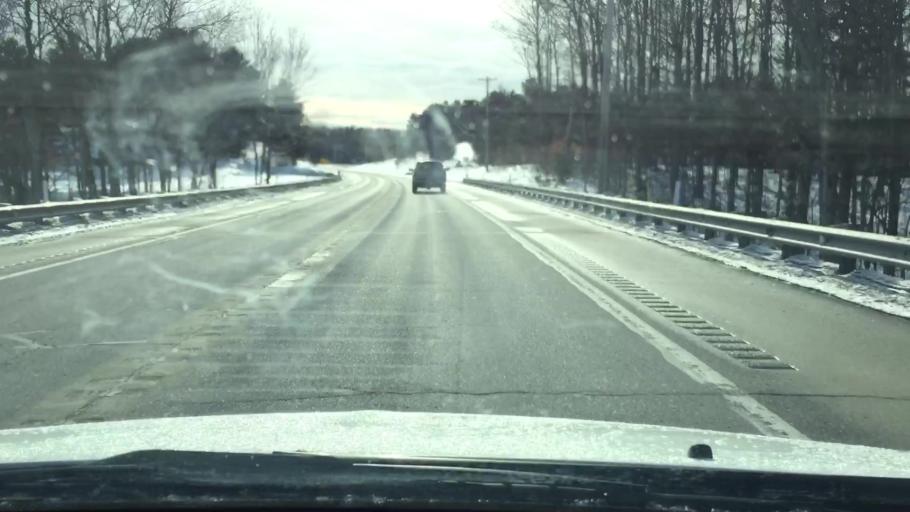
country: US
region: Michigan
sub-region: Wexford County
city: Manton
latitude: 44.5814
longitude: -85.3606
